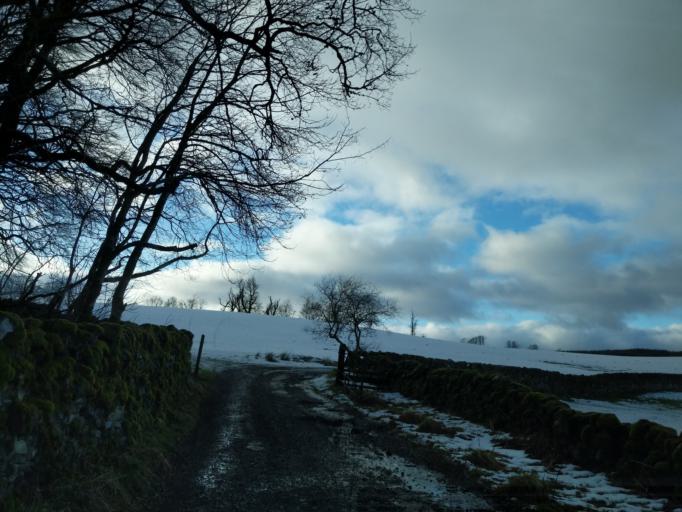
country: GB
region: Scotland
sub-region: Dumfries and Galloway
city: Moffat
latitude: 55.3217
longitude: -3.4806
